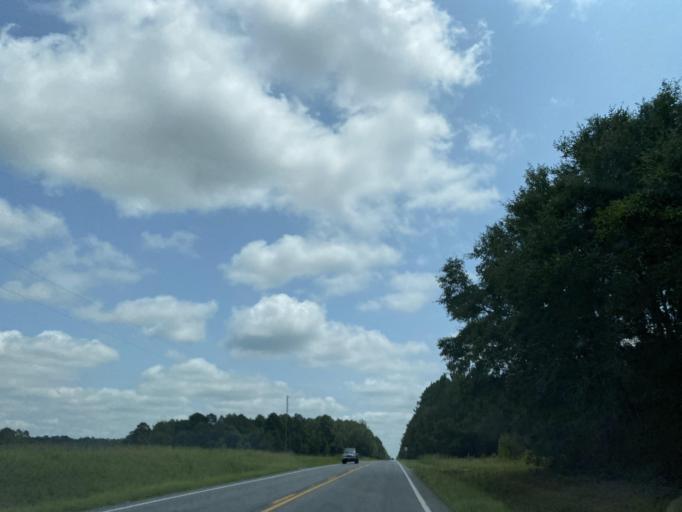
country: US
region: Georgia
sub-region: Jeff Davis County
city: Hazlehurst
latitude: 31.7090
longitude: -82.5176
